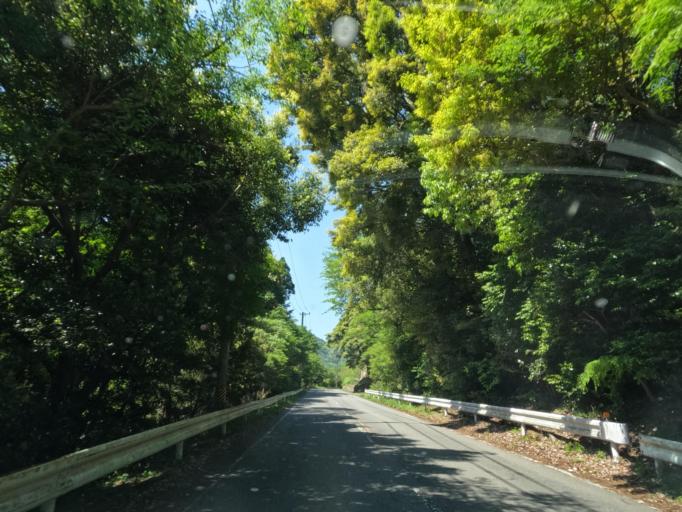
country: JP
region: Mie
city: Komono
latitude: 35.0212
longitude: 136.4539
